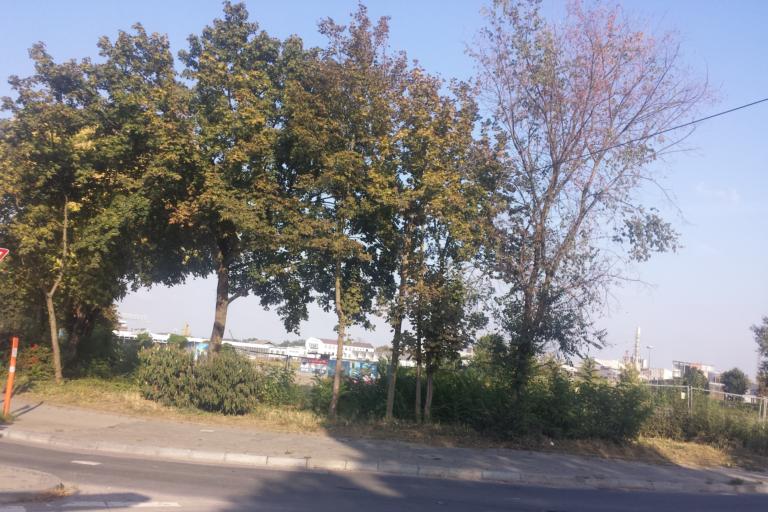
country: DE
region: Rheinland-Pfalz
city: Gartenstadt
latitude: 49.4551
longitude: 8.4270
